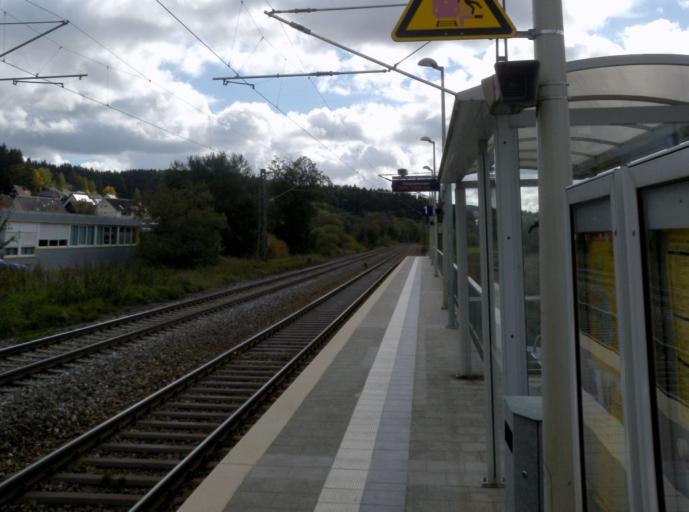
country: DE
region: Baden-Wuerttemberg
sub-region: Freiburg Region
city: Villingen-Schwenningen
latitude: 48.0309
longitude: 8.4693
